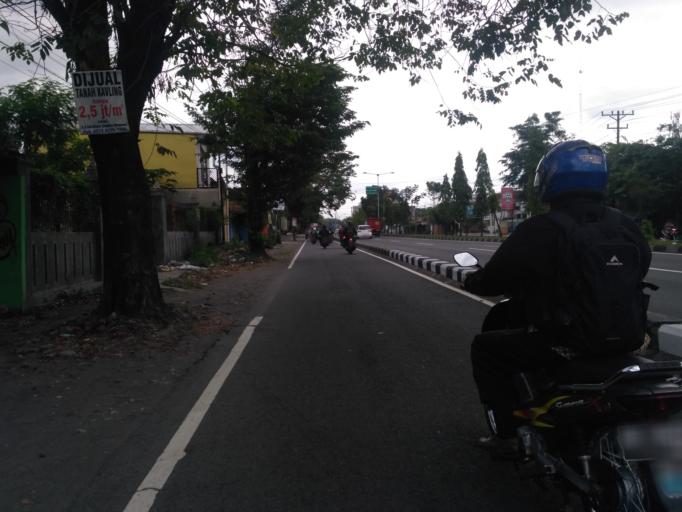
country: ID
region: Daerah Istimewa Yogyakarta
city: Melati
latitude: -7.7518
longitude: 110.3738
